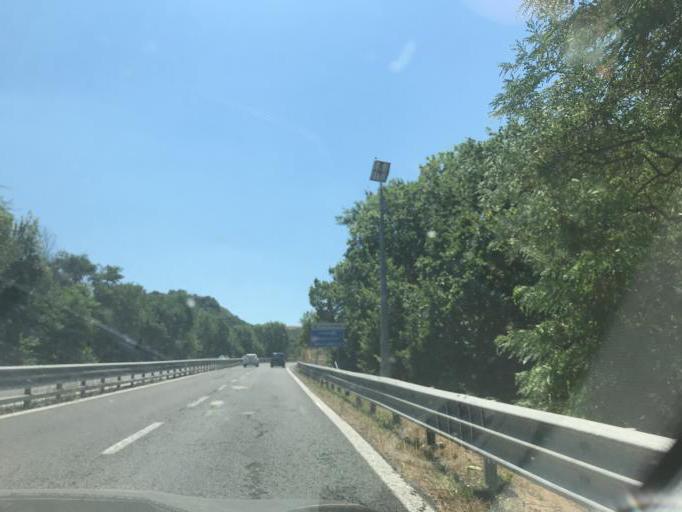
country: IT
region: Sardinia
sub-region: Provincia di Sassari
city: Codrongianos
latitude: 40.6626
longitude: 8.6695
